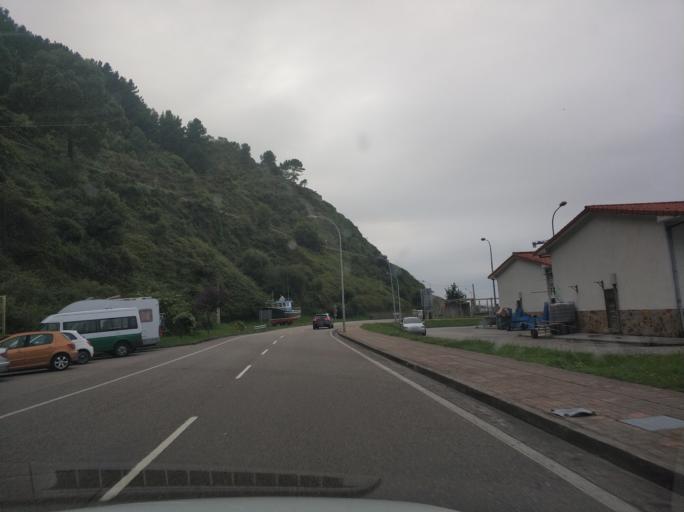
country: ES
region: Asturias
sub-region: Province of Asturias
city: Cudillero
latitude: 43.5656
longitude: -6.1519
